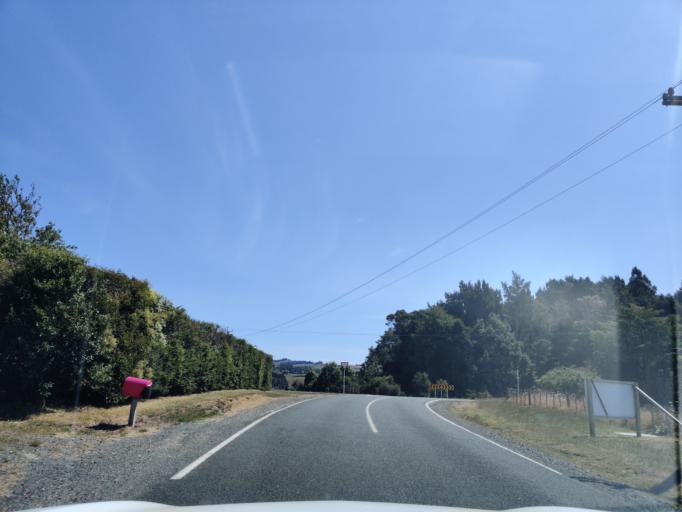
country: NZ
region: Auckland
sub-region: Auckland
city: Red Hill
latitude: -37.0690
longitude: 175.0712
